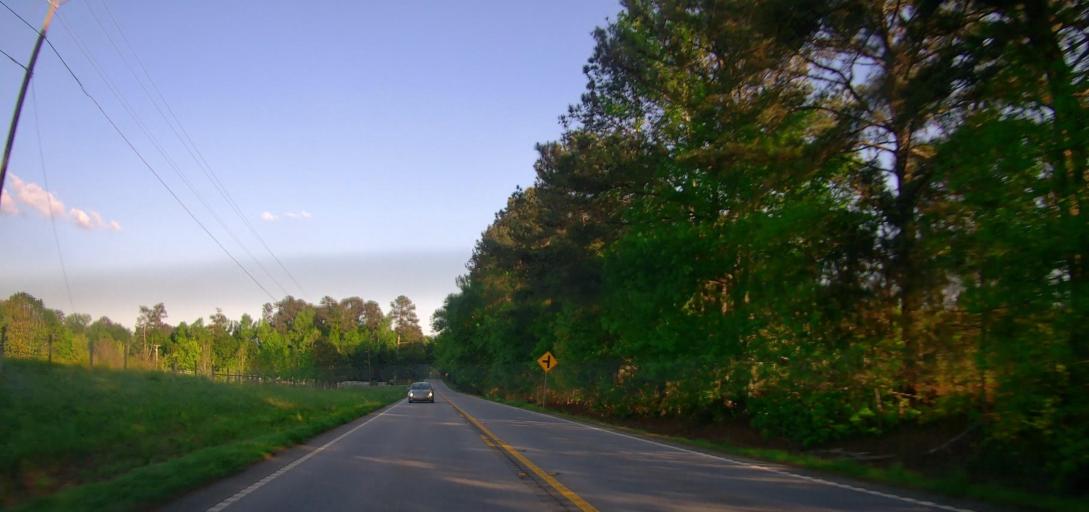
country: US
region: Georgia
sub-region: Walton County
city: Social Circle
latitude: 33.5477
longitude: -83.7327
